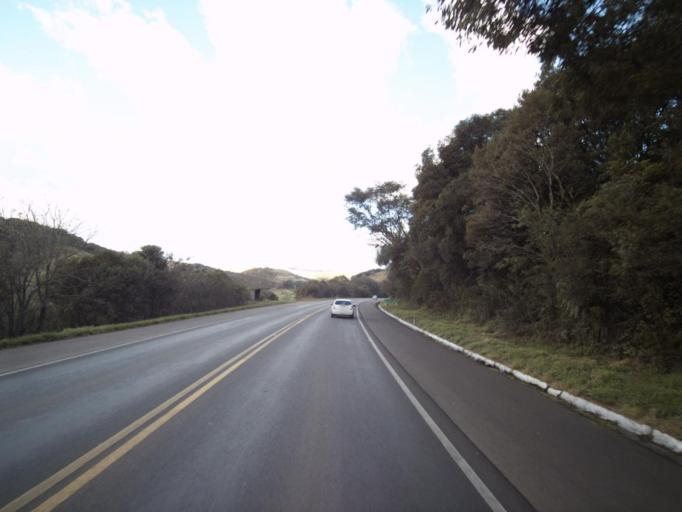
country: BR
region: Santa Catarina
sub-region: Campos Novos
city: Campos Novos
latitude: -27.3127
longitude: -51.3703
